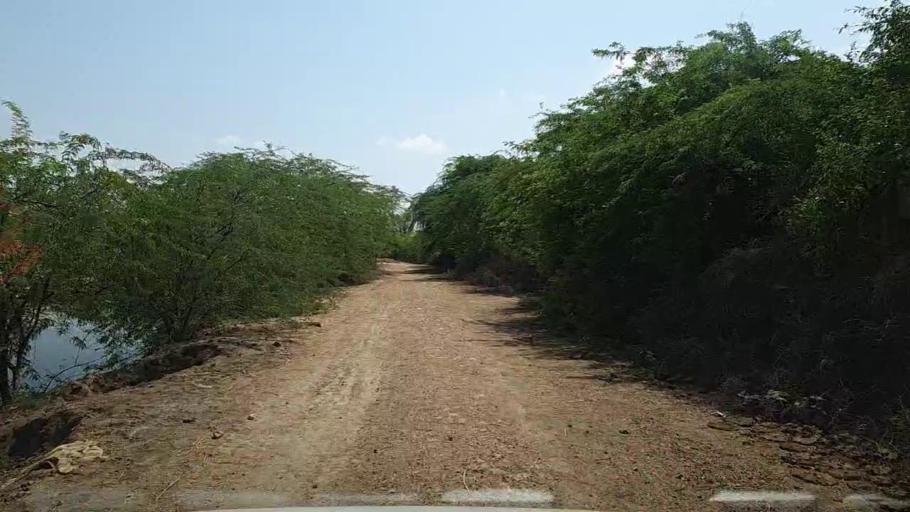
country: PK
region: Sindh
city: Kario
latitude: 24.6959
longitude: 68.6157
